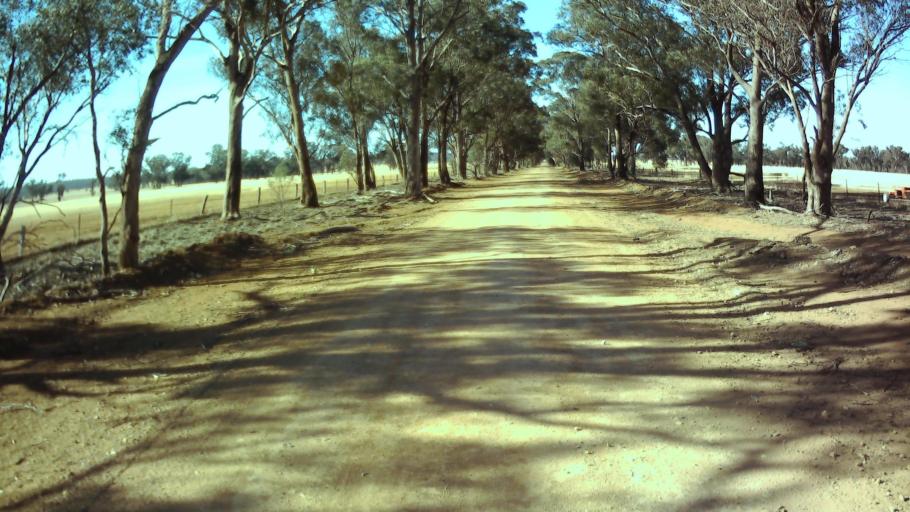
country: AU
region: New South Wales
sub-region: Weddin
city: Grenfell
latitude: -33.8351
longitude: 147.8727
